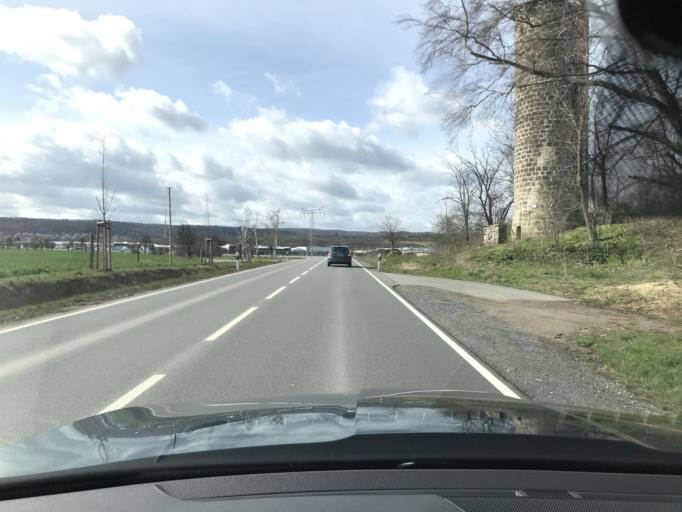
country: DE
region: Saxony-Anhalt
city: Rieder
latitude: 51.7433
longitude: 11.1518
